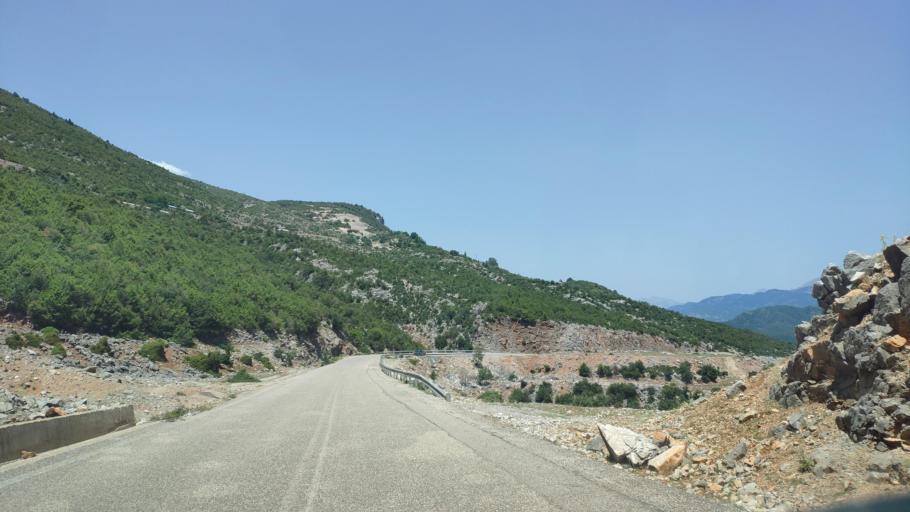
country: GR
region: Thessaly
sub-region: Nomos Kardhitsas
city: Anthiro
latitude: 39.1398
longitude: 21.3885
